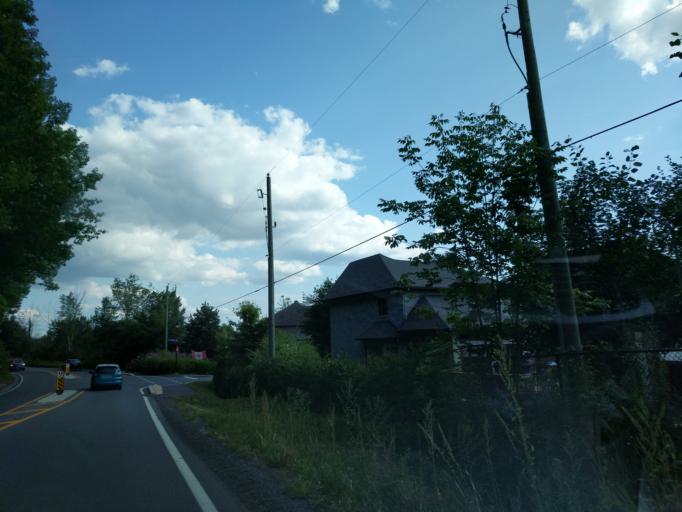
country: CA
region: Quebec
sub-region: Outaouais
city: Gatineau
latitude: 45.4521
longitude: -75.7928
